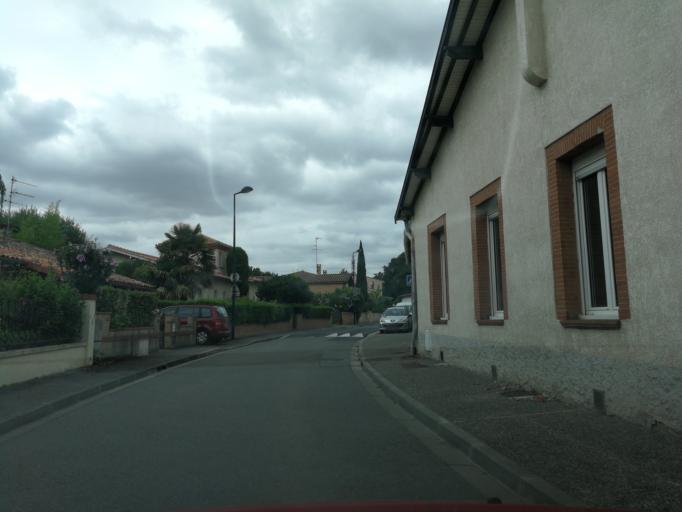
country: FR
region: Midi-Pyrenees
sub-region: Departement de la Haute-Garonne
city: Auzeville-Tolosane
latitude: 43.5301
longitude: 1.4791
